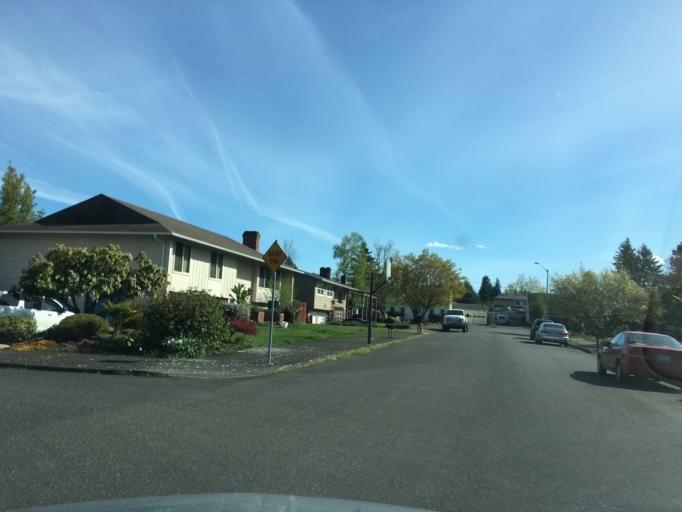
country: US
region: Oregon
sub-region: Multnomah County
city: Lents
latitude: 45.5421
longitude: -122.5282
